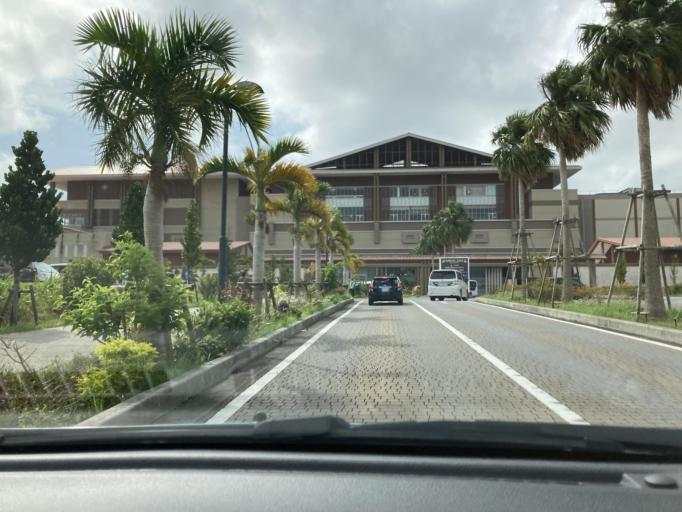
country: JP
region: Okinawa
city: Okinawa
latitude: 26.3158
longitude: 127.7965
